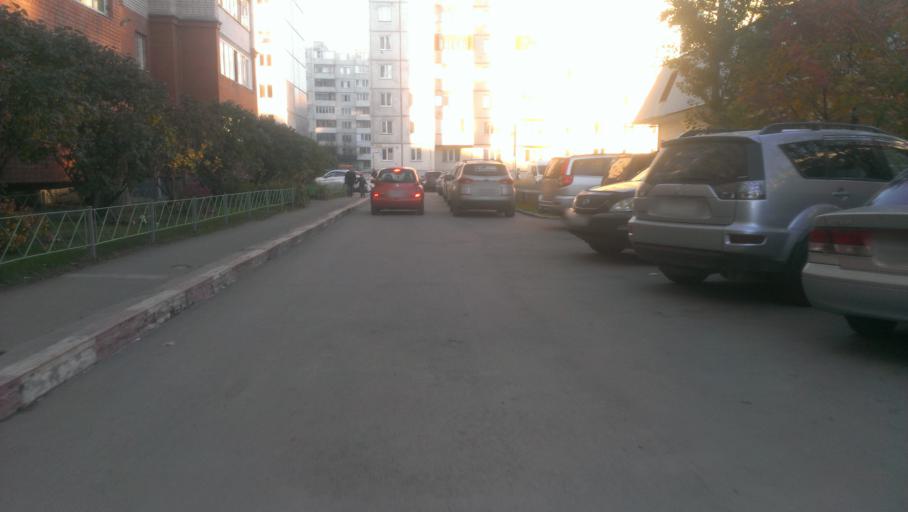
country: RU
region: Altai Krai
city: Novosilikatnyy
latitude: 53.3413
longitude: 83.6719
